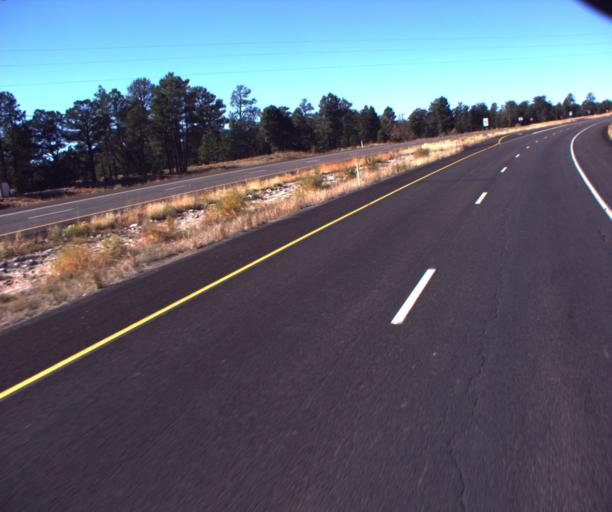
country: US
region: Arizona
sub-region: Apache County
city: Saint Michaels
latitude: 35.6580
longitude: -109.1558
